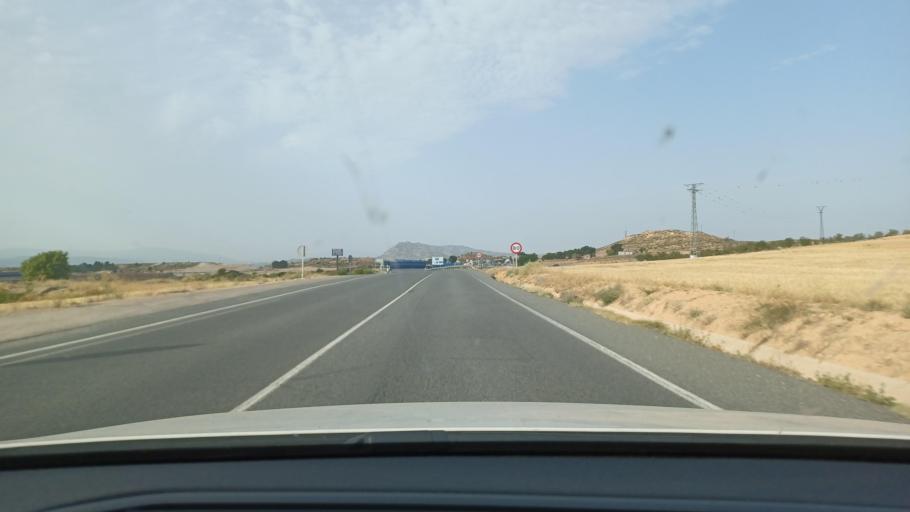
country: ES
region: Castille-La Mancha
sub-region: Provincia de Albacete
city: Caudete
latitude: 38.7350
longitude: -0.9352
